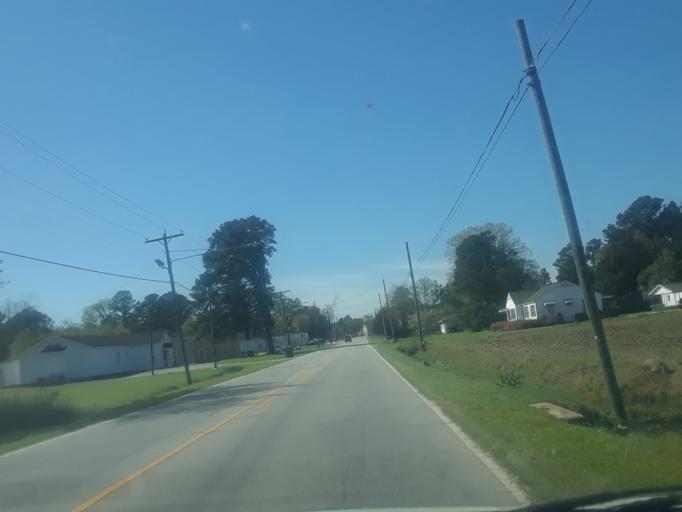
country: US
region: North Carolina
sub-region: Harnett County
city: Erwin
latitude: 35.3201
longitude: -78.6555
